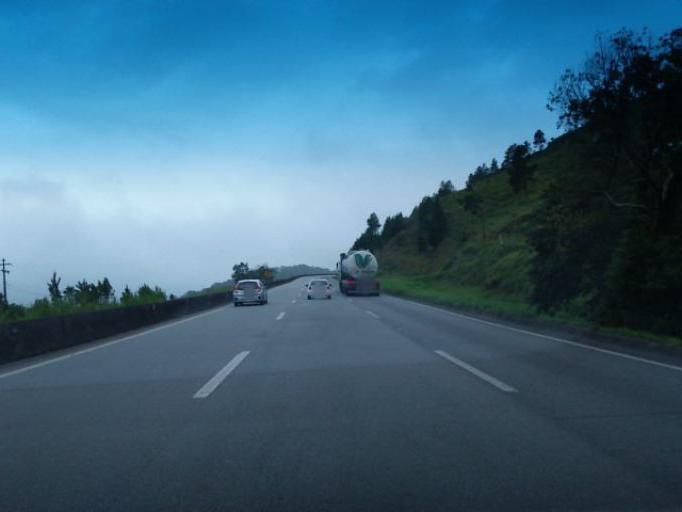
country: BR
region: Parana
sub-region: Campina Grande Do Sul
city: Campina Grande do Sul
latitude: -25.1086
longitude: -48.8262
